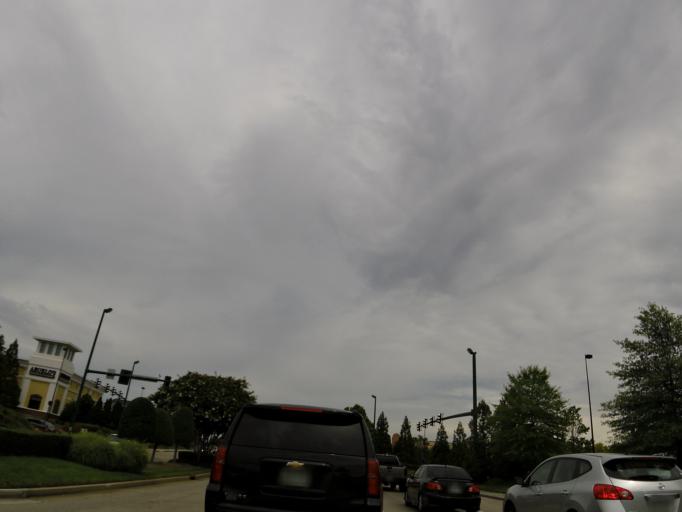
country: US
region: Tennessee
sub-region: Knox County
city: Farragut
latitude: 35.8998
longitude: -84.1588
